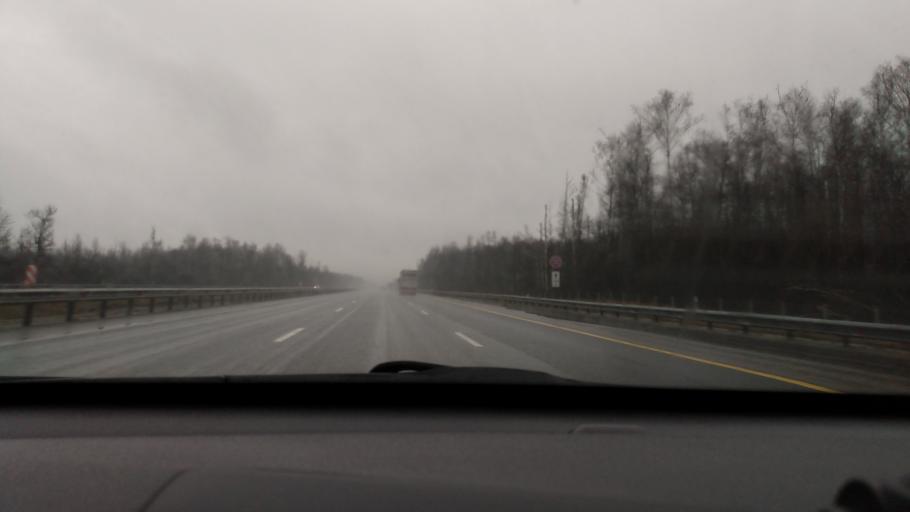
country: RU
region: Moskovskaya
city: Zhilevo
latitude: 54.9467
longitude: 37.9864
